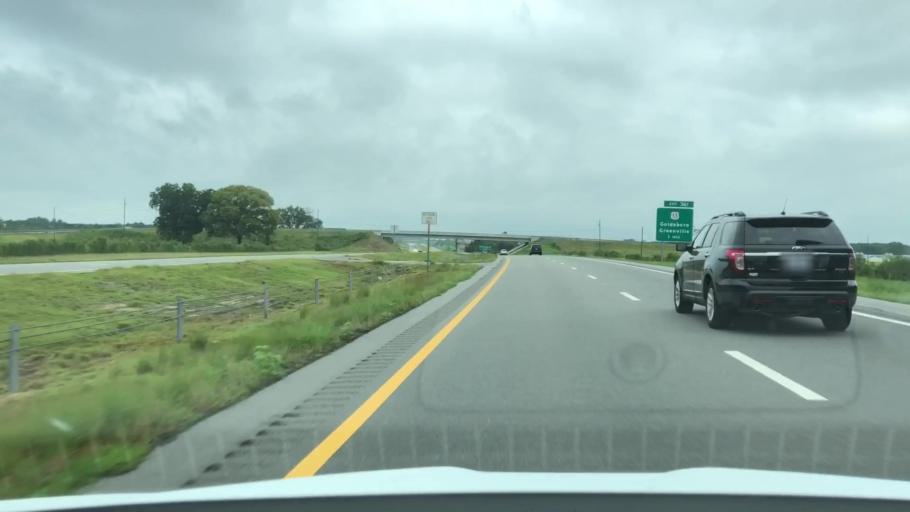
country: US
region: North Carolina
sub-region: Wayne County
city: Elroy
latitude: 35.4022
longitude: -77.8755
